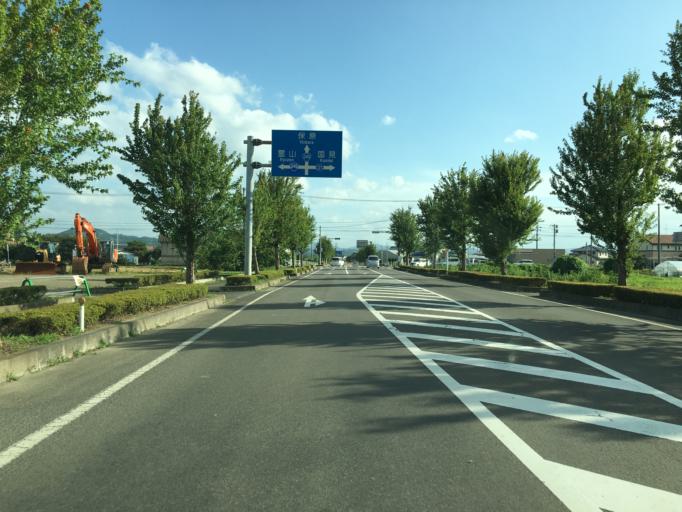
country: JP
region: Fukushima
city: Yanagawamachi-saiwaicho
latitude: 37.8512
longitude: 140.5924
